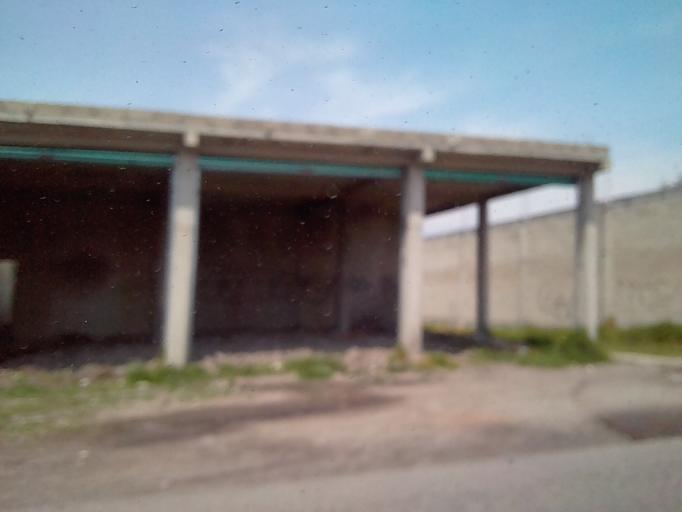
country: MX
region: Mexico
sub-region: Toluca
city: Guadalupe Totoltepec
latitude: 19.3447
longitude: -99.5566
